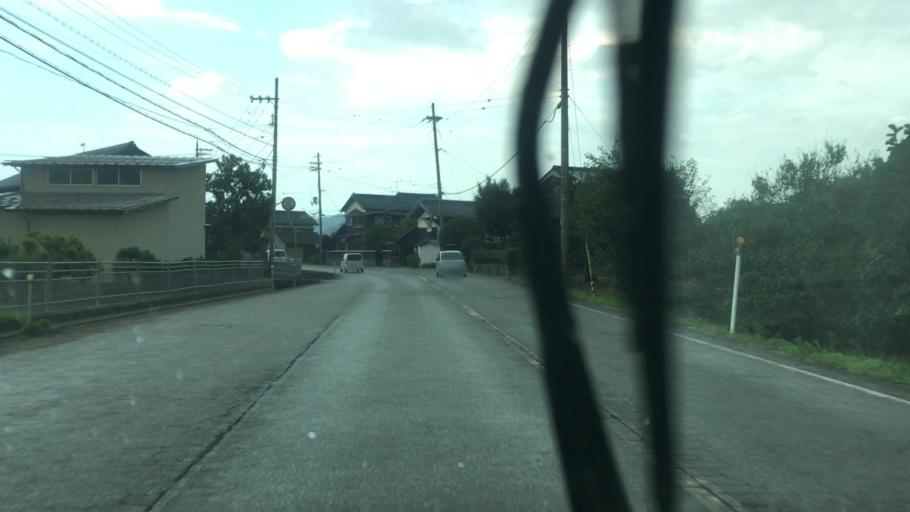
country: JP
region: Hyogo
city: Toyooka
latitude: 35.4999
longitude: 134.8189
